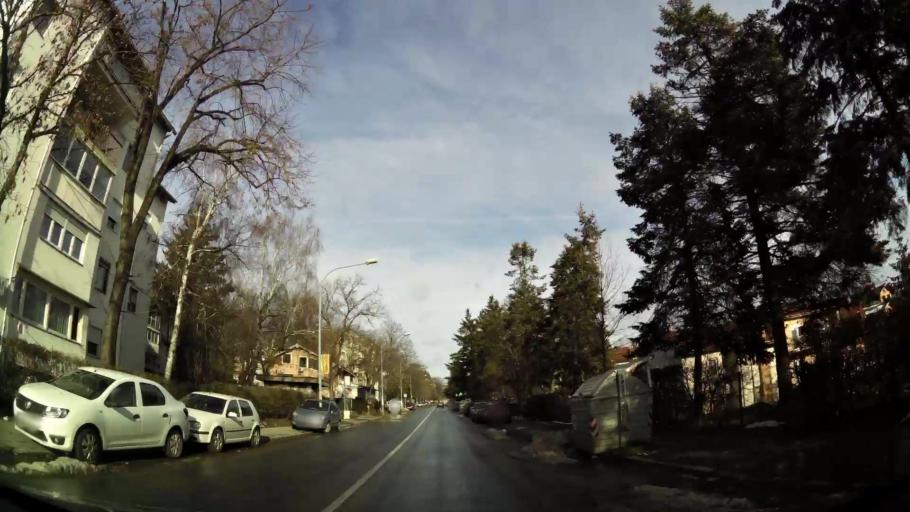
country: RS
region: Central Serbia
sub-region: Belgrade
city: Rakovica
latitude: 44.7244
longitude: 20.4220
